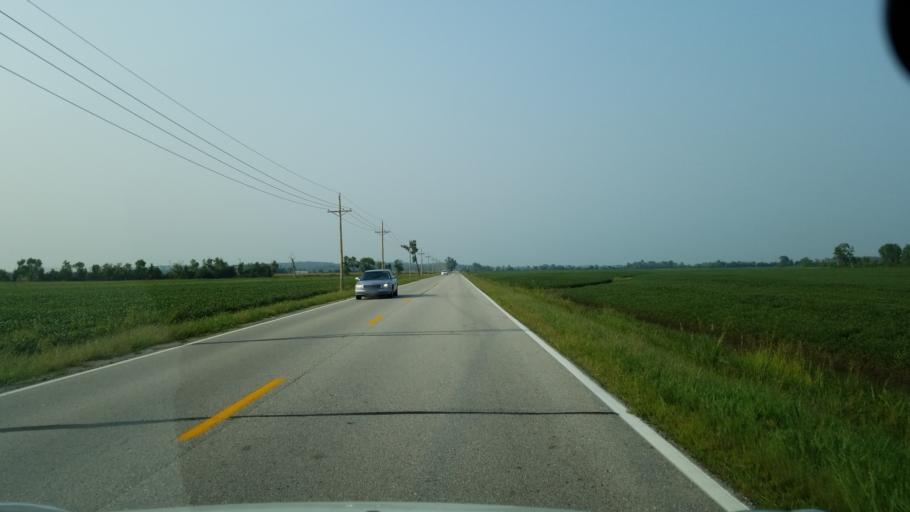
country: US
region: Nebraska
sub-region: Sarpy County
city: Offutt Air Force Base
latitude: 41.0933
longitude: -95.8898
